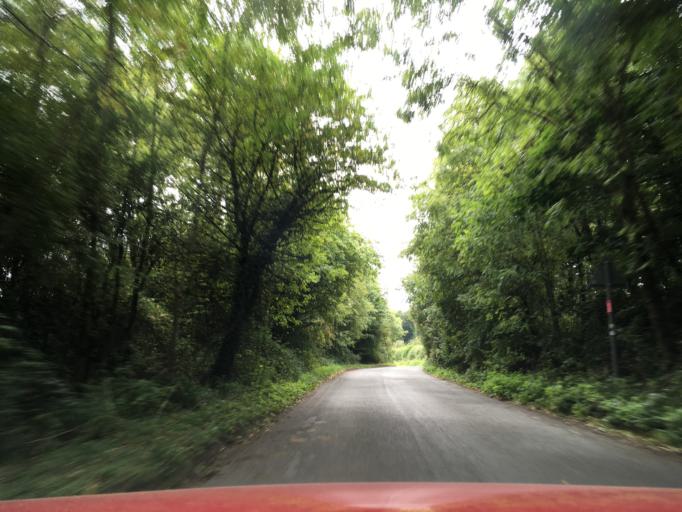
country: GB
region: England
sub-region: Gloucestershire
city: Berkeley
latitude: 51.6719
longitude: -2.4210
